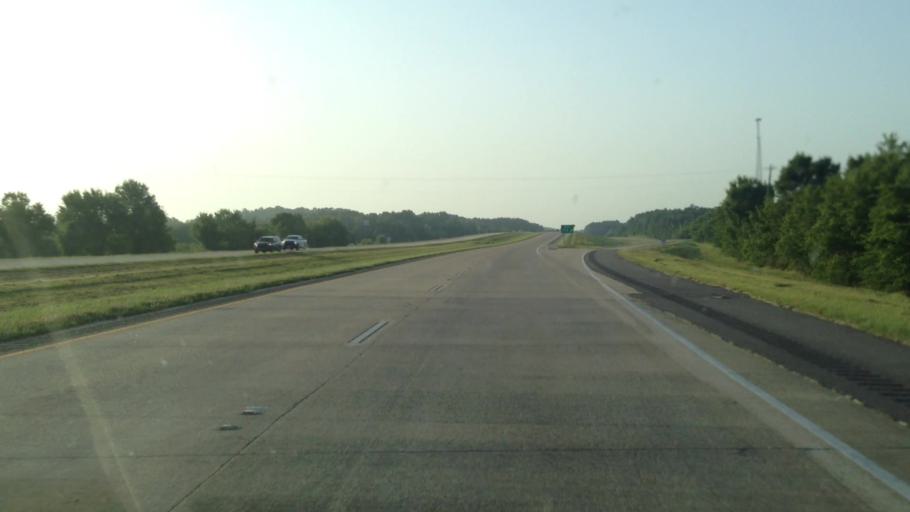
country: US
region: Louisiana
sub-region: Grant Parish
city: Colfax
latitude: 31.4985
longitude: -92.8673
